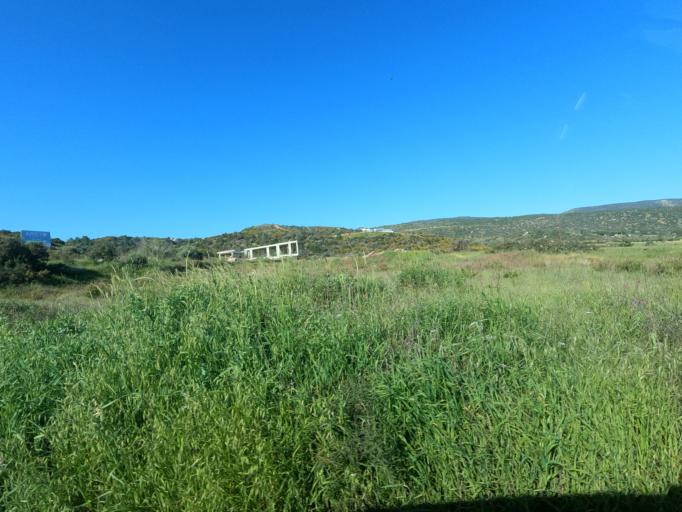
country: CY
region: Pafos
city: Polis
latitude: 35.0420
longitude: 32.3657
